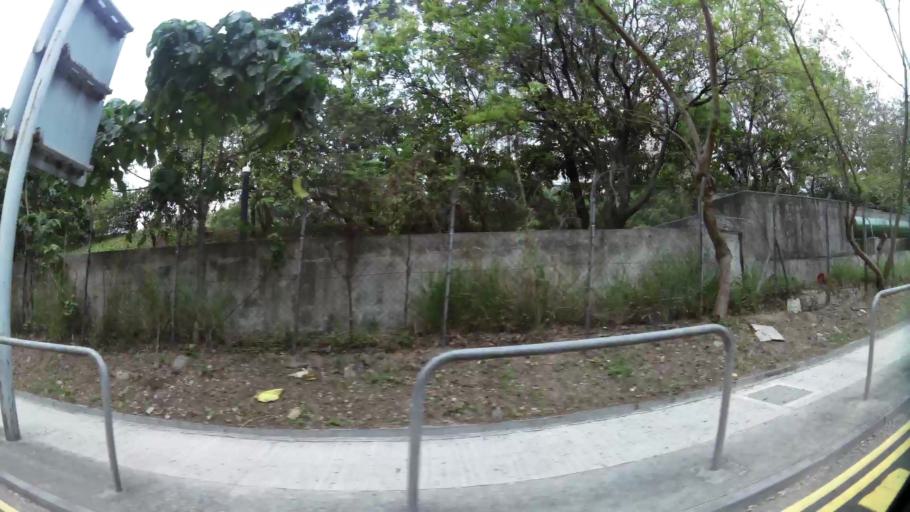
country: HK
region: Kowloon City
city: Kowloon
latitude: 22.3141
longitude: 114.2388
